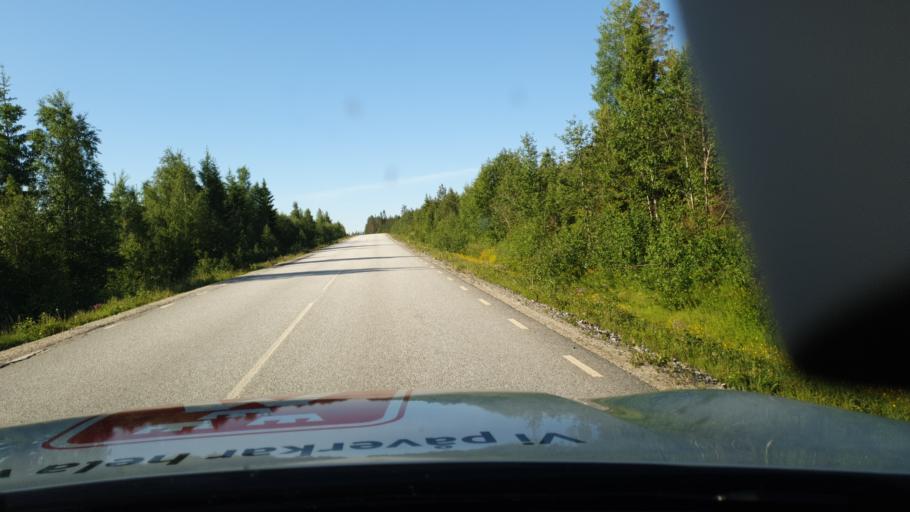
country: SE
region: Vaesterbotten
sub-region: Bjurholms Kommun
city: Bjurholm
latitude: 64.1821
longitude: 19.4021
